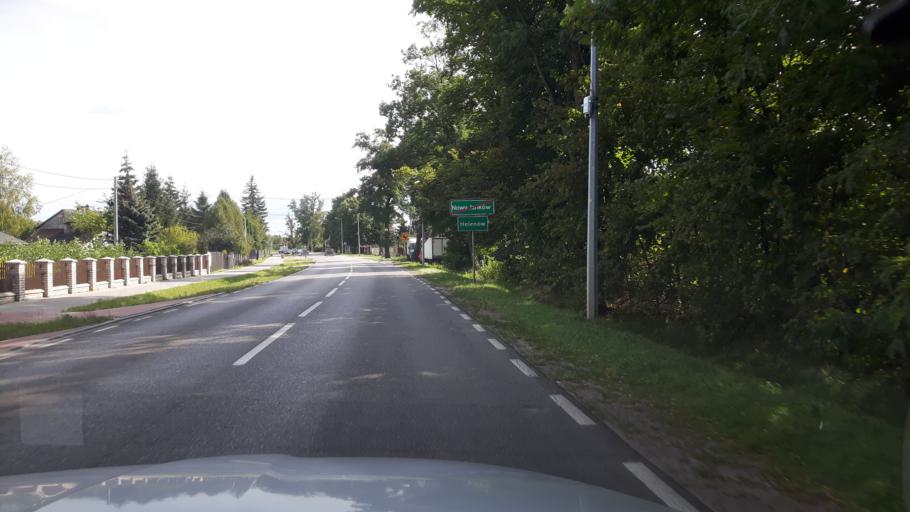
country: PL
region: Masovian Voivodeship
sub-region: Powiat wolominski
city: Kobylka
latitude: 52.3782
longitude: 21.2141
